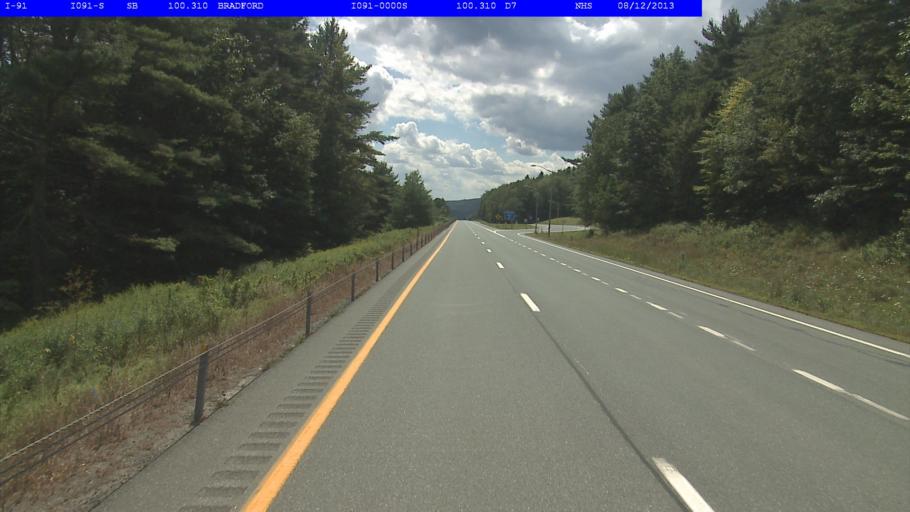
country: US
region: New Hampshire
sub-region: Grafton County
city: Haverhill
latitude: 44.0196
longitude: -72.1195
